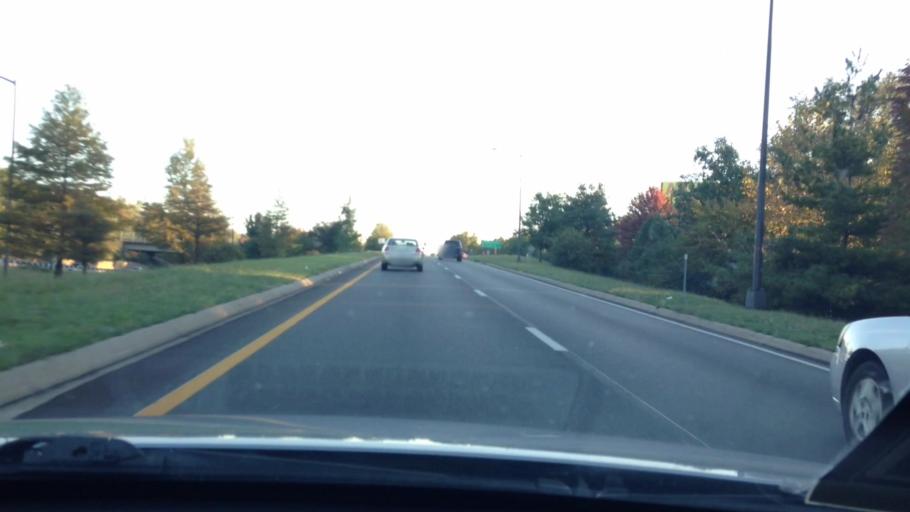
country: US
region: Kansas
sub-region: Johnson County
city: Mission Hills
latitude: 39.0147
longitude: -94.5550
